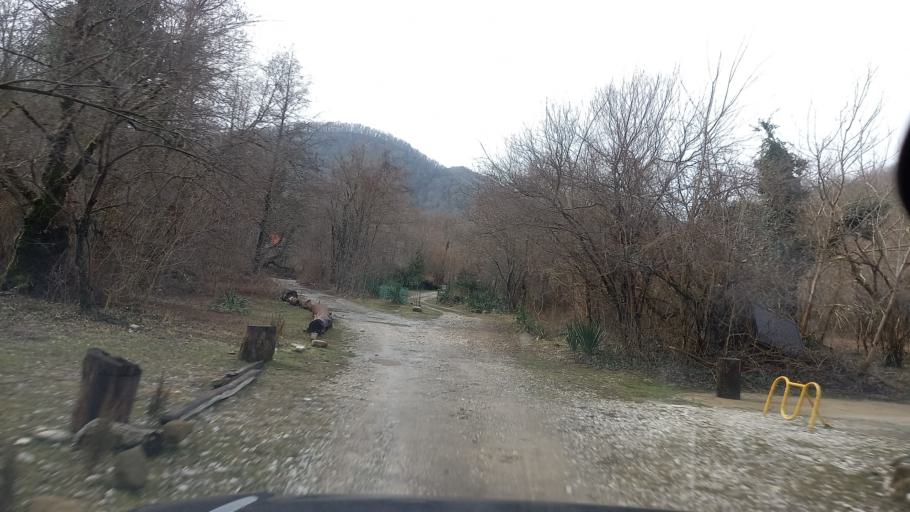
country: RU
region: Krasnodarskiy
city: Dzhubga
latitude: 44.4144
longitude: 38.7205
